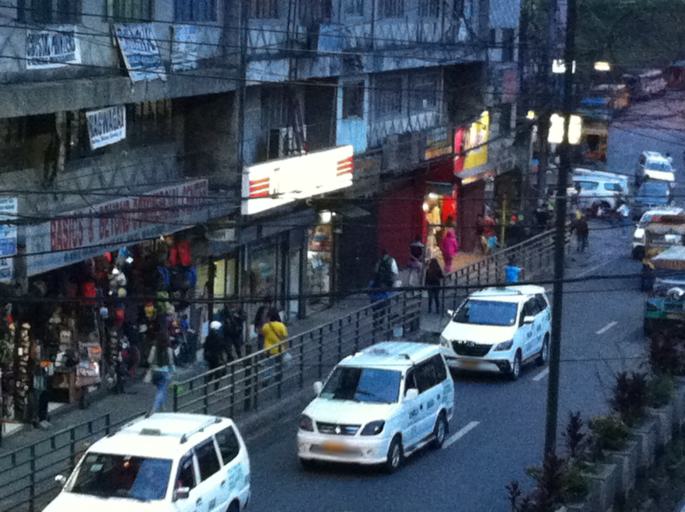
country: PH
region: Cordillera
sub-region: Baguio City
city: Baguio
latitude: 16.4169
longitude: 120.5961
